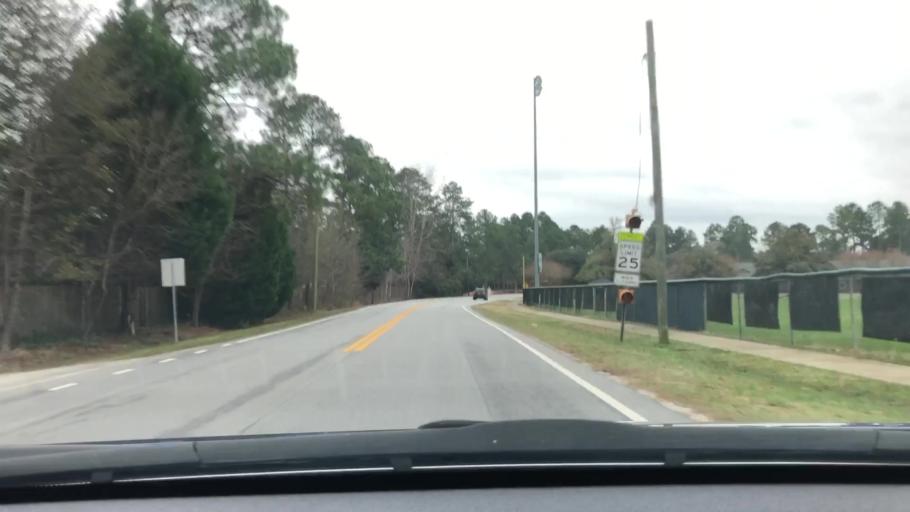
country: US
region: South Carolina
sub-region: Sumter County
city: Cherryvale
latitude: 33.9373
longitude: -80.4046
